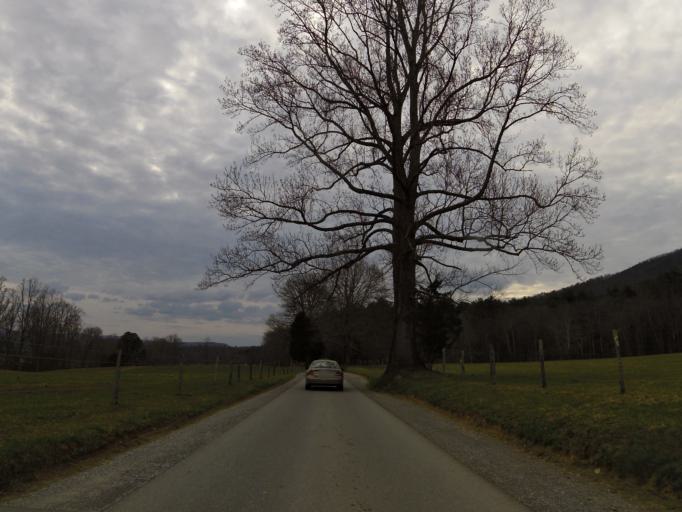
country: US
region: Tennessee
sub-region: Blount County
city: Wildwood
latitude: 35.6068
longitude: -83.7844
